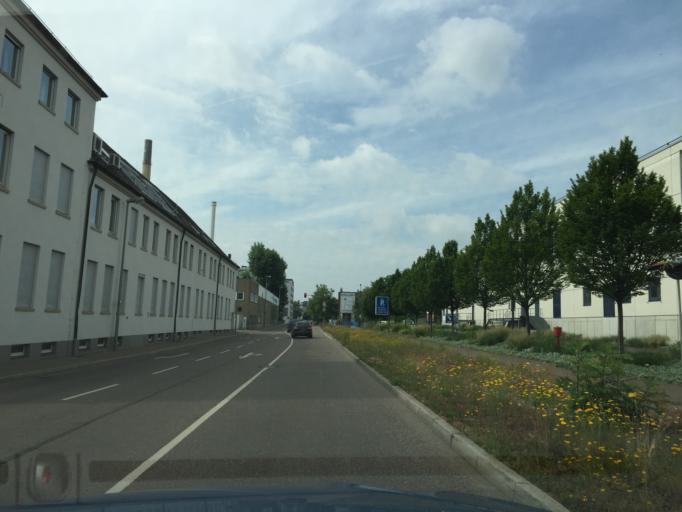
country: DE
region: Baden-Wuerttemberg
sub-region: Tuebingen Region
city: Ulm
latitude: 48.4002
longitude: 9.9648
